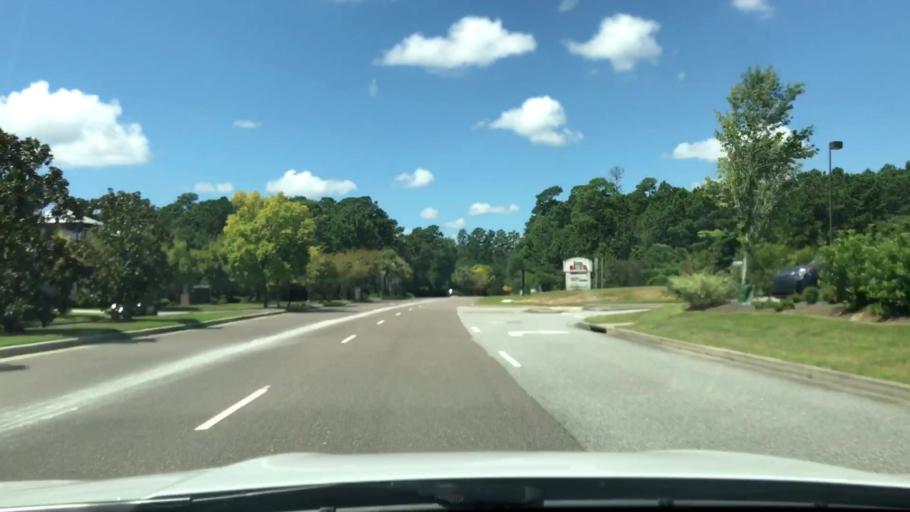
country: US
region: South Carolina
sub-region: Berkeley County
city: Hanahan
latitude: 32.9334
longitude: -79.9982
